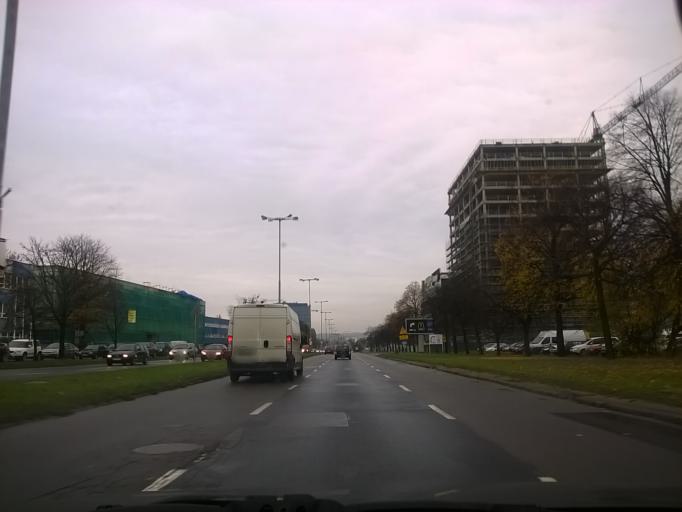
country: PL
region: Pomeranian Voivodeship
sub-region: Sopot
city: Sopot
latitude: 54.4051
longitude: 18.5712
